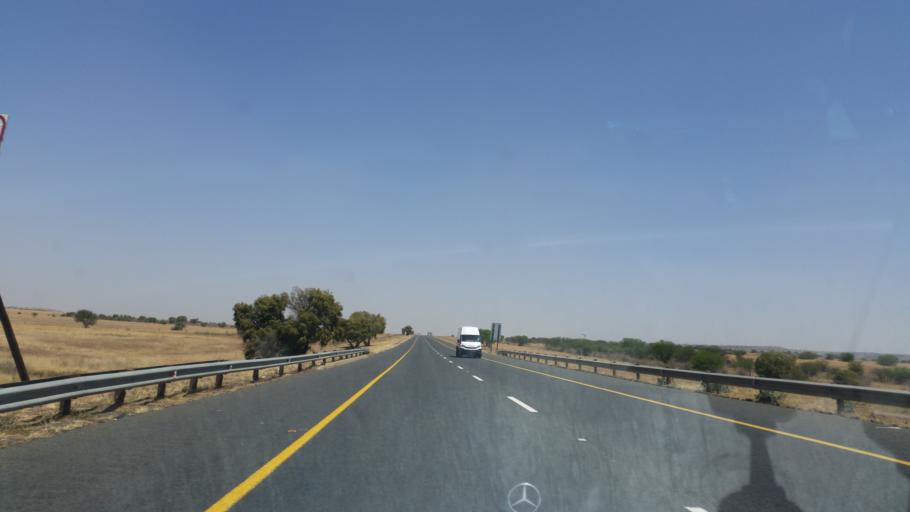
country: ZA
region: Orange Free State
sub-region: Lejweleputswa District Municipality
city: Winburg
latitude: -28.6746
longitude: 26.8391
